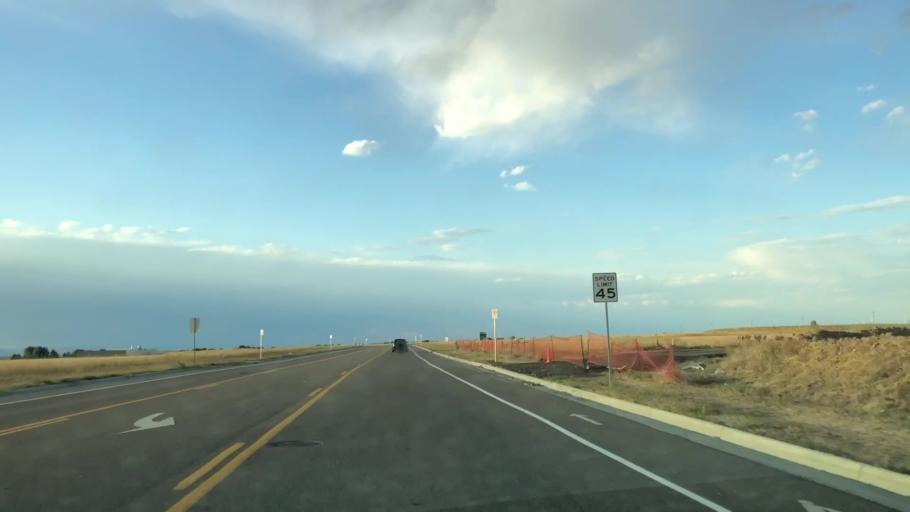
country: US
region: Colorado
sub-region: Larimer County
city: Loveland
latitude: 40.4390
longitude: -104.9960
